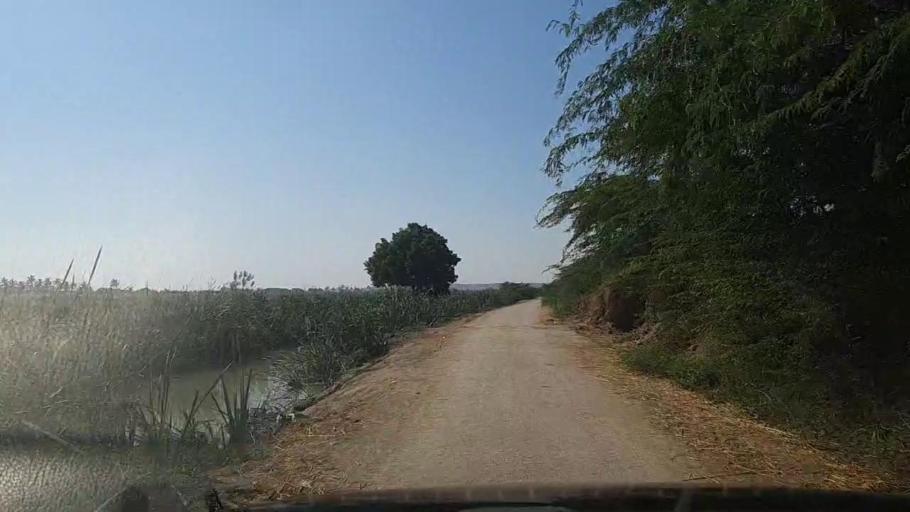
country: PK
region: Sindh
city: Thatta
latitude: 24.6357
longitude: 67.8746
